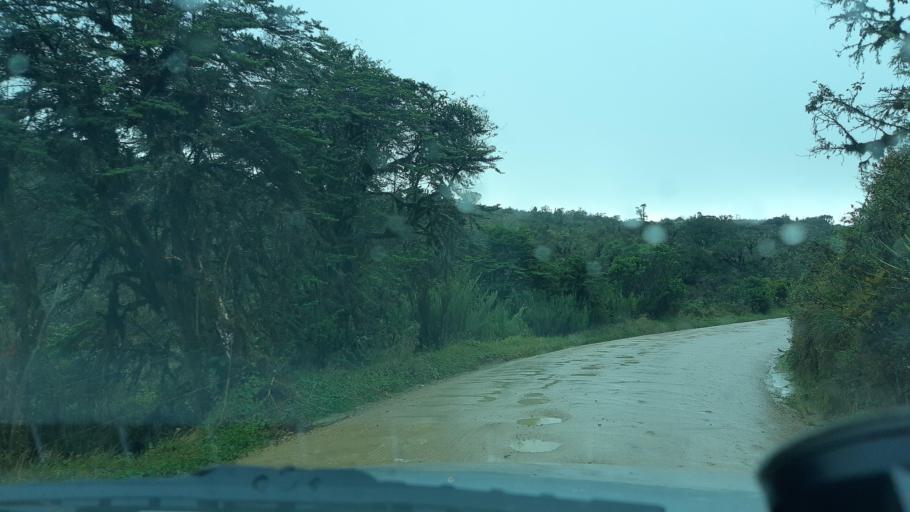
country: CO
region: Cundinamarca
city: Villapinzon
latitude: 5.2157
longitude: -73.5266
